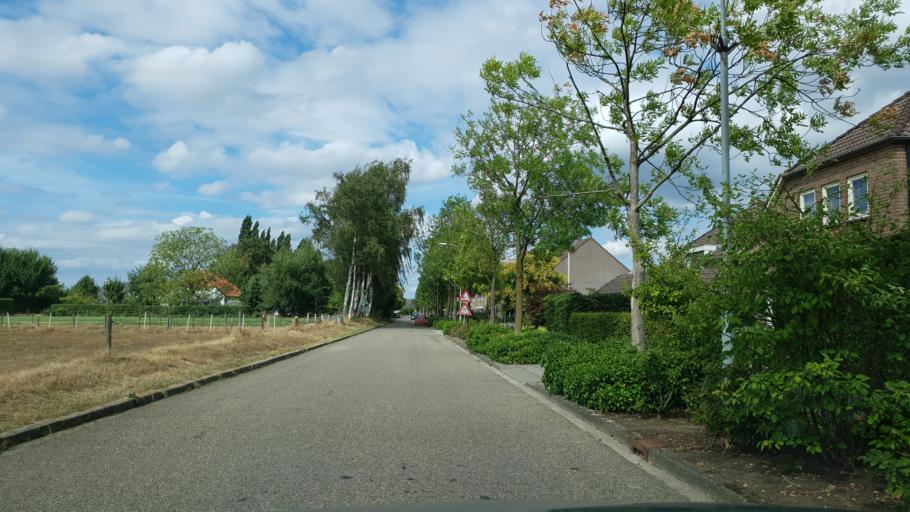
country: NL
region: North Brabant
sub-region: Gemeente Grave
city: Grave
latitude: 51.7584
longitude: 5.7820
